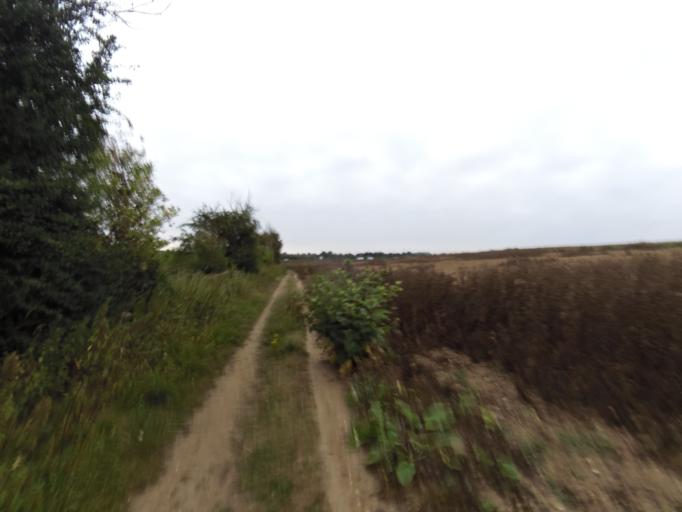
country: GB
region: England
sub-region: Hertfordshire
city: Radlett
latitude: 51.7149
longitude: -0.3132
